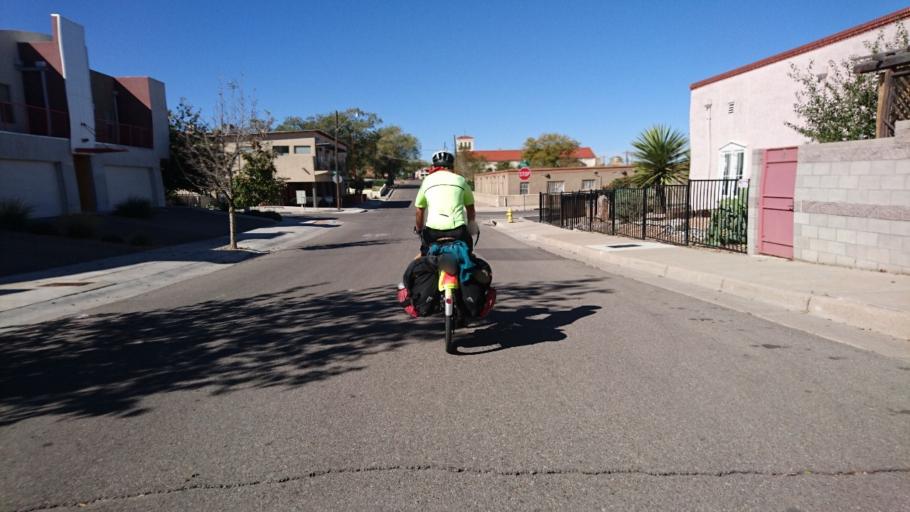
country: US
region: New Mexico
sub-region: Bernalillo County
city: Albuquerque
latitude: 35.0785
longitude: -106.6006
